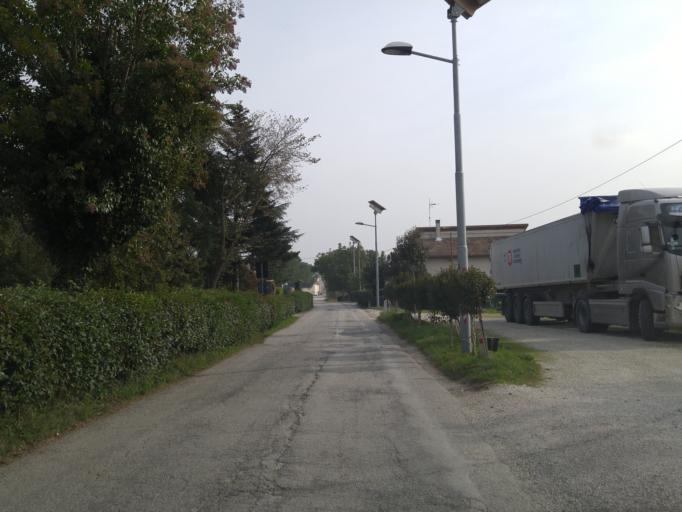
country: IT
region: The Marches
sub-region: Provincia di Pesaro e Urbino
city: Lucrezia
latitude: 43.7682
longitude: 12.9425
